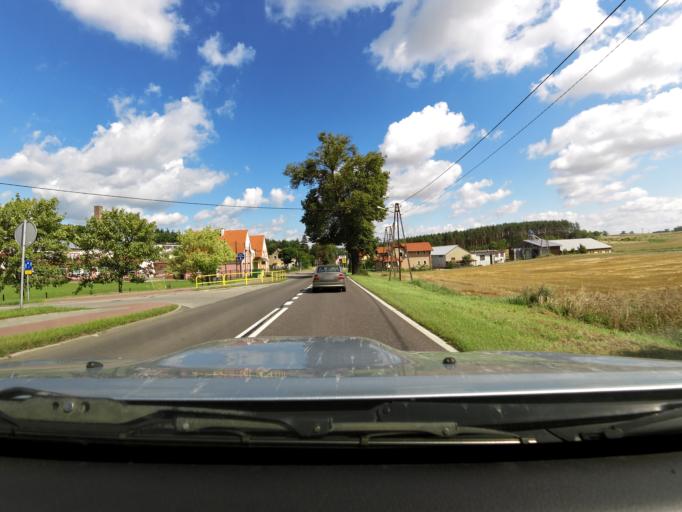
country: PL
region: Pomeranian Voivodeship
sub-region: Powiat kwidzynski
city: Ryjewo
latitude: 53.7843
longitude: 18.9620
